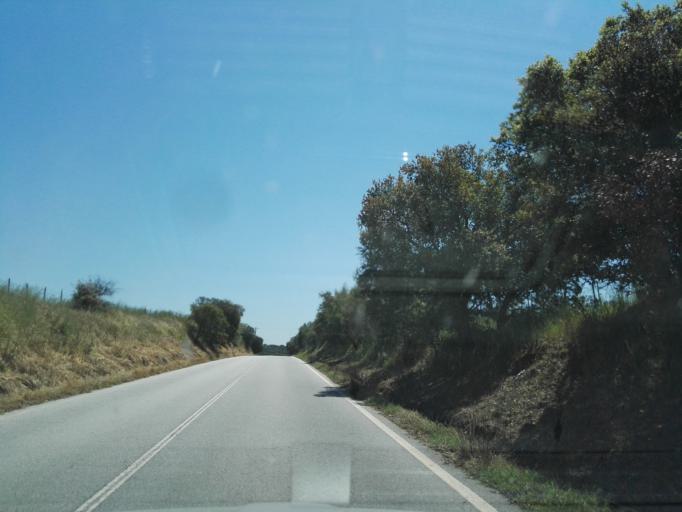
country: PT
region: Portalegre
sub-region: Arronches
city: Arronches
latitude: 39.0054
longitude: -7.2300
